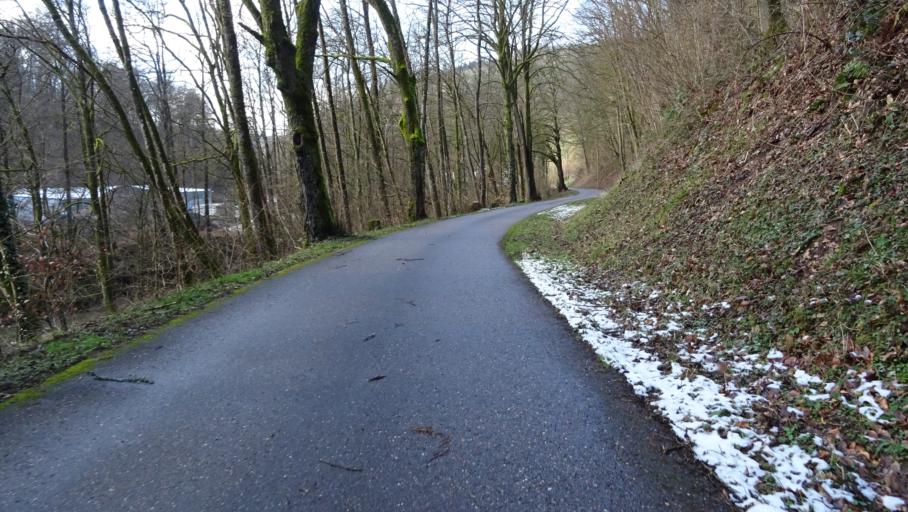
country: DE
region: Baden-Wuerttemberg
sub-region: Karlsruhe Region
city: Neckargerach
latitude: 49.4044
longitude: 9.0838
